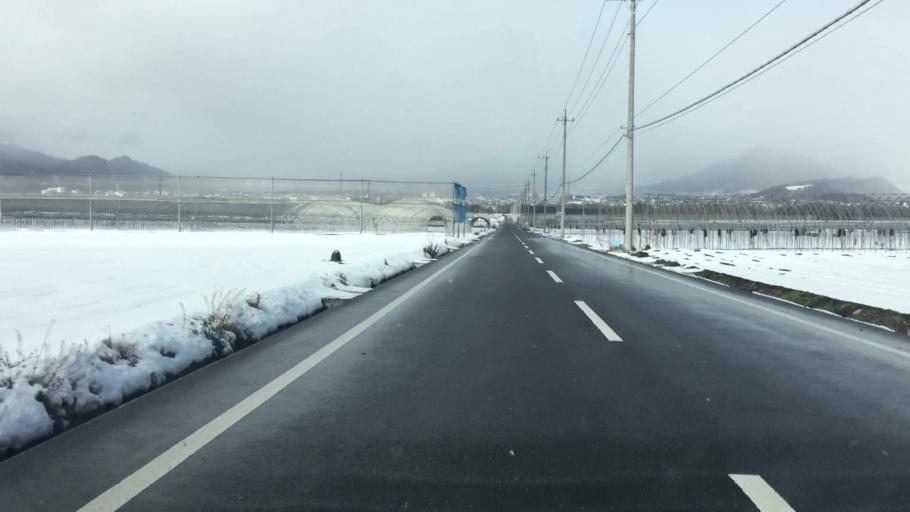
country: JP
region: Gunma
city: Numata
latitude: 36.6291
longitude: 139.0911
